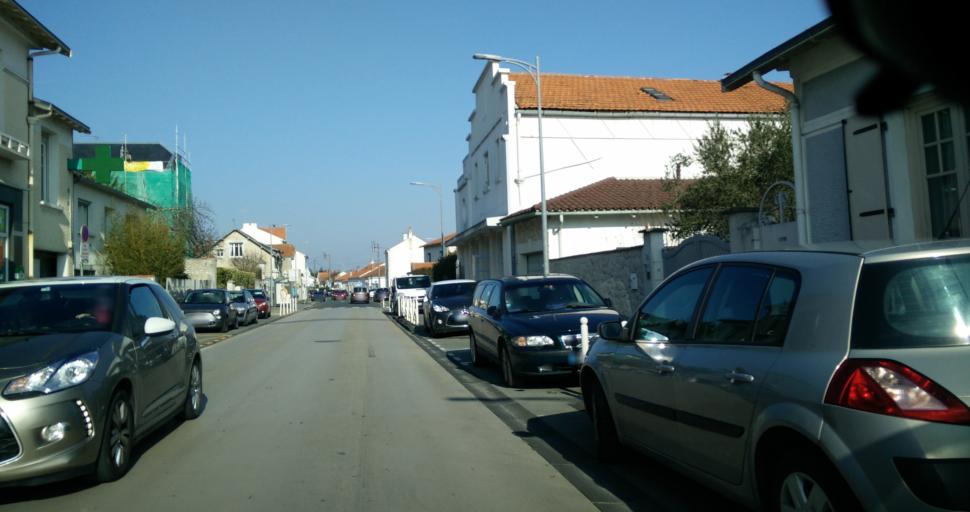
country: FR
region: Poitou-Charentes
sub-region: Departement de la Charente-Maritime
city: La Rochelle
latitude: 46.1702
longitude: -1.1585
